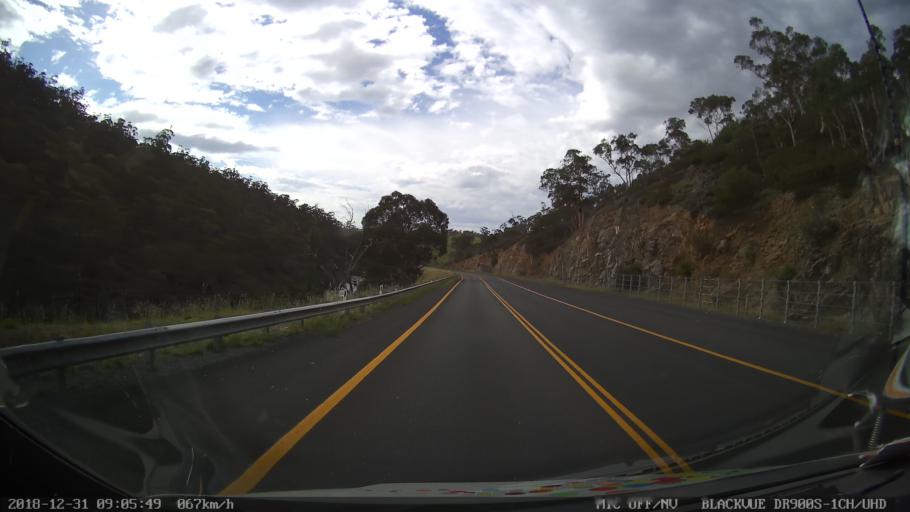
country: AU
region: New South Wales
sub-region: Snowy River
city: Jindabyne
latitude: -36.3669
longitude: 148.5881
